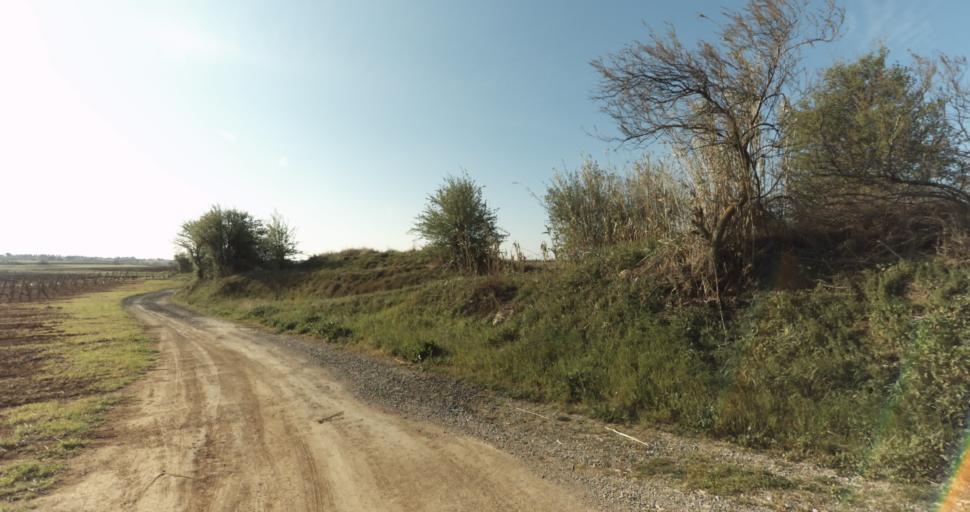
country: FR
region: Languedoc-Roussillon
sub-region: Departement de l'Herault
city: Marseillan
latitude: 43.3703
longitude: 3.5122
